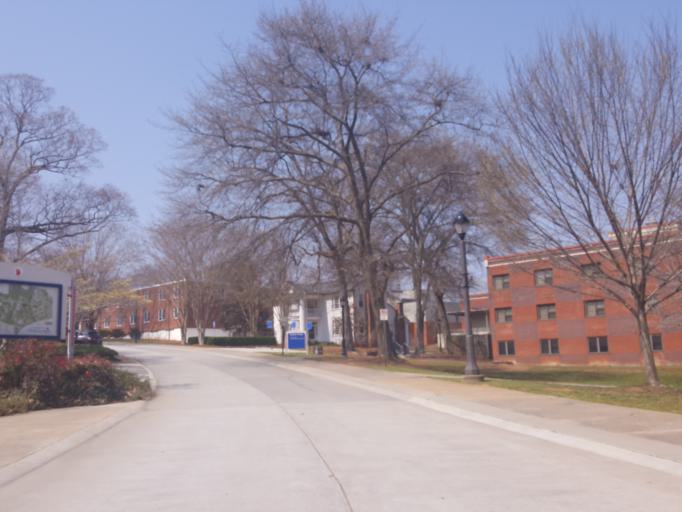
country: US
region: Georgia
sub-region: Carroll County
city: Carrollton
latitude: 33.5716
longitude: -85.0947
